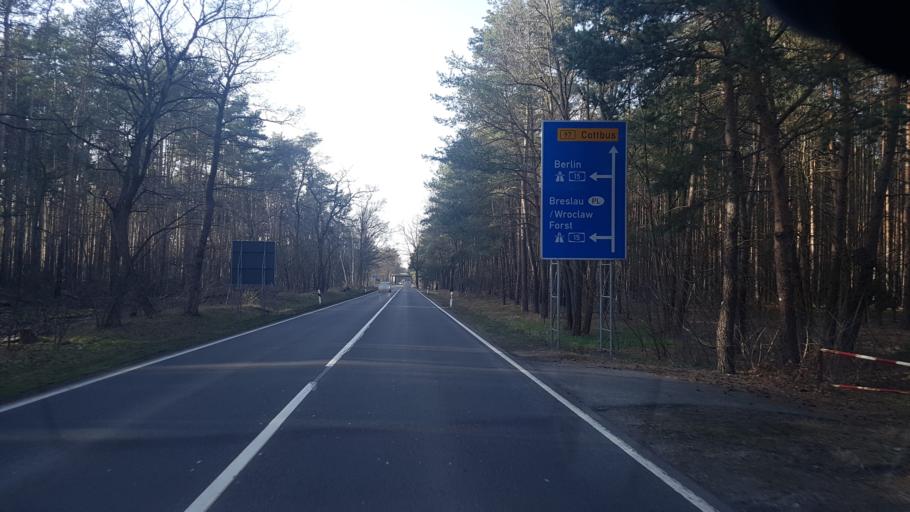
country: DE
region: Brandenburg
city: Heinersbruck
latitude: 51.7096
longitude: 14.4695
